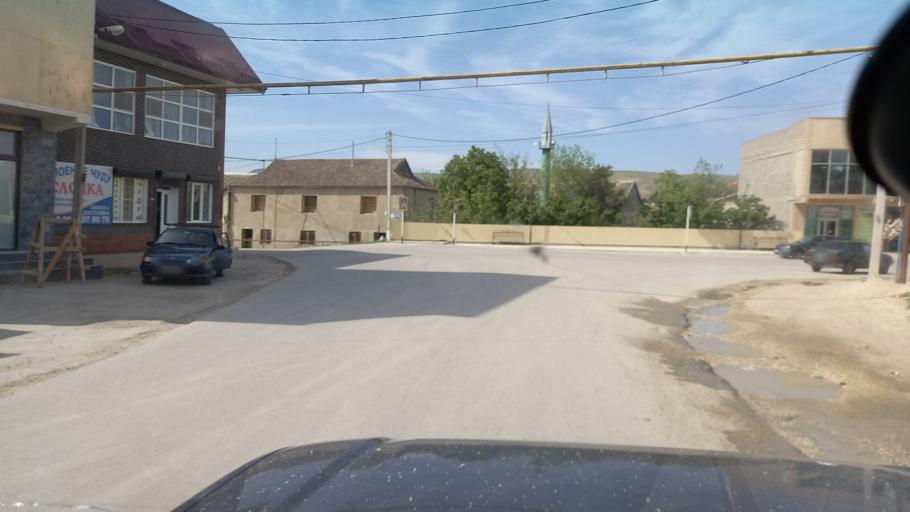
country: RU
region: Dagestan
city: Karabudakhkent
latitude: 42.7081
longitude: 47.5709
